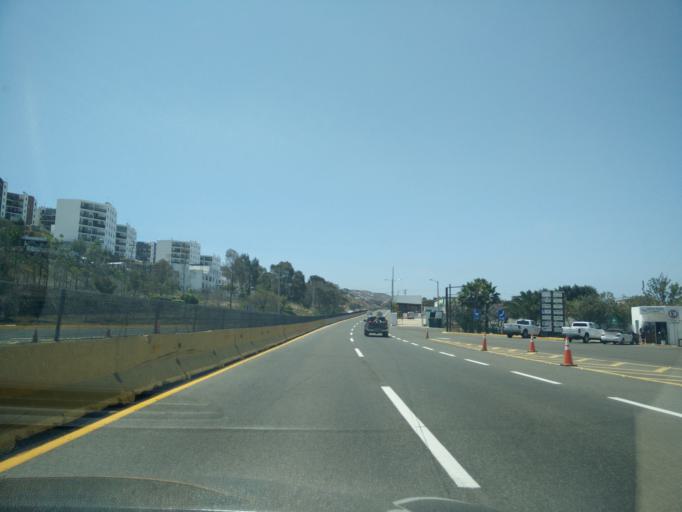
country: US
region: California
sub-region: San Diego County
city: Imperial Beach
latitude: 32.5266
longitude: -117.1078
